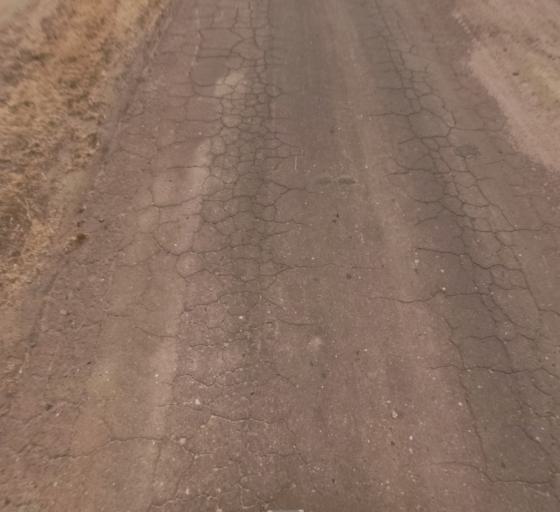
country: US
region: California
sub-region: Madera County
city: Madera Acres
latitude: 37.0908
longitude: -120.1085
